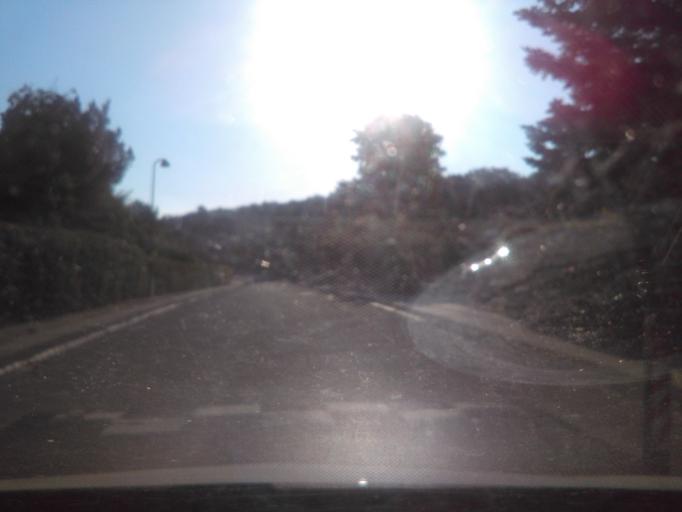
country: DK
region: Capital Region
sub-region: Fureso Kommune
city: Vaerlose
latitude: 55.7741
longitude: 12.3729
